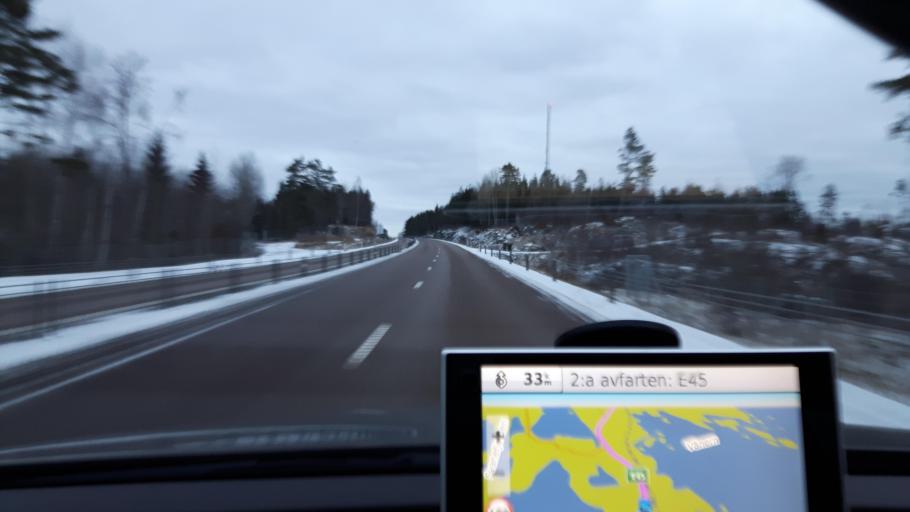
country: SE
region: Vaestra Goetaland
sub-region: Melleruds Kommun
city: Mellerud
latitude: 58.7965
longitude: 12.5223
